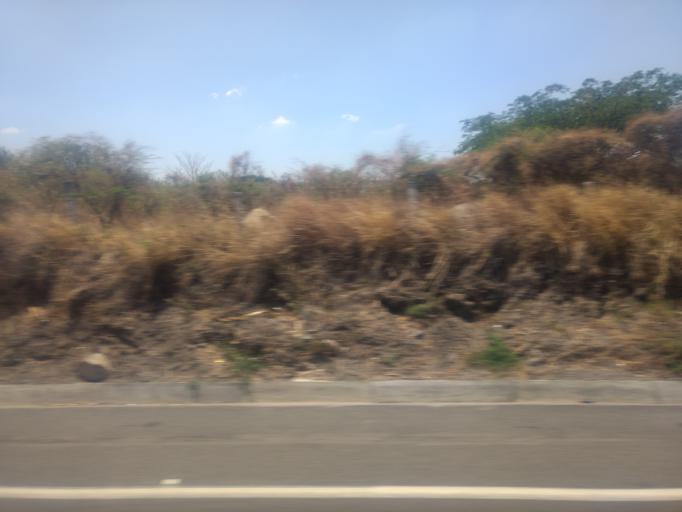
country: MX
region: Colima
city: Cuauhtemoc
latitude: 19.3278
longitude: -103.5892
